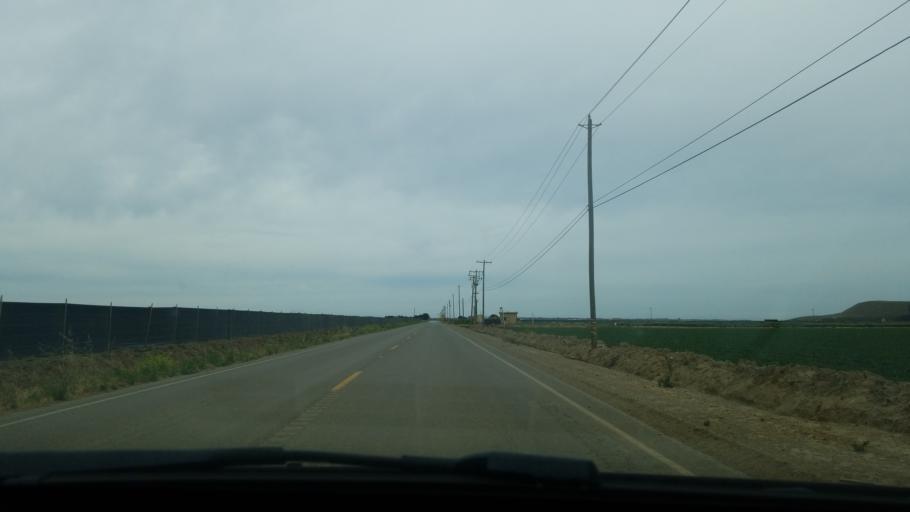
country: US
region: California
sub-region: San Luis Obispo County
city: Nipomo
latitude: 35.0049
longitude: -120.5118
